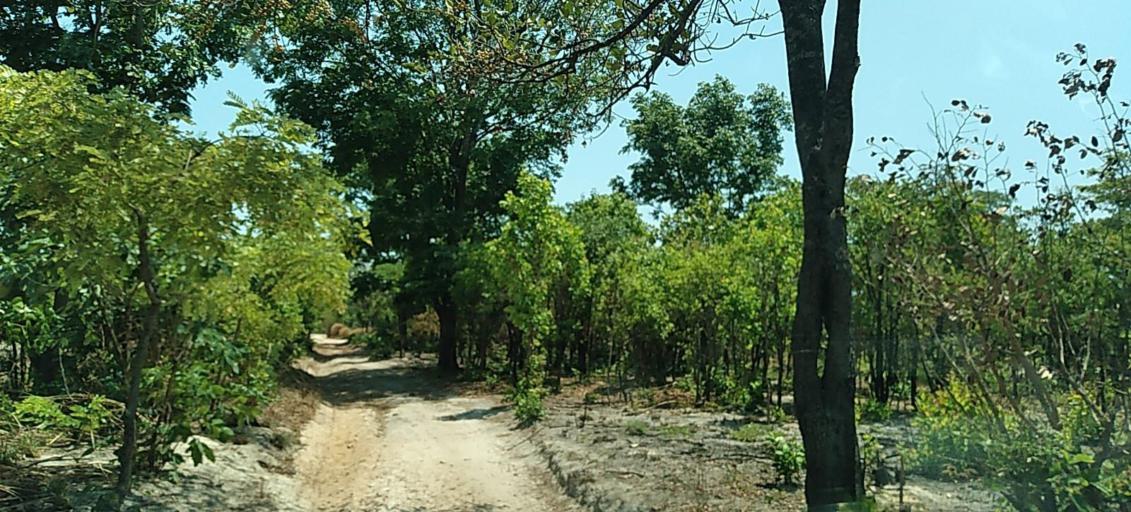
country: ZM
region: Copperbelt
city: Luanshya
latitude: -12.9836
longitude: 28.3294
